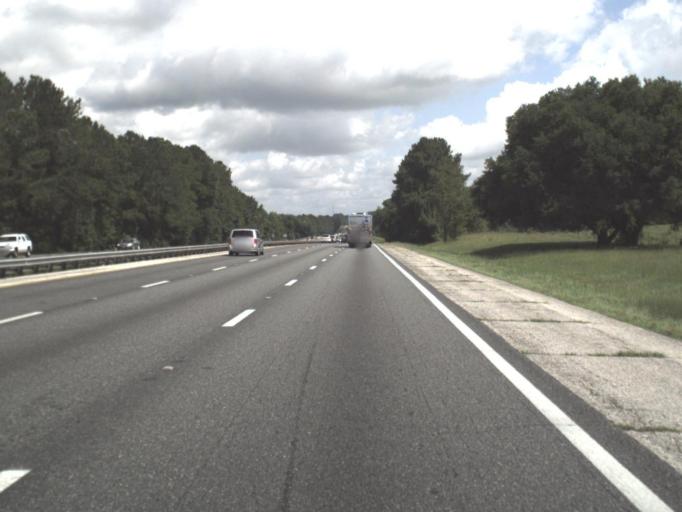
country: US
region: Florida
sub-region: Alachua County
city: High Springs
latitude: 29.9208
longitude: -82.5560
